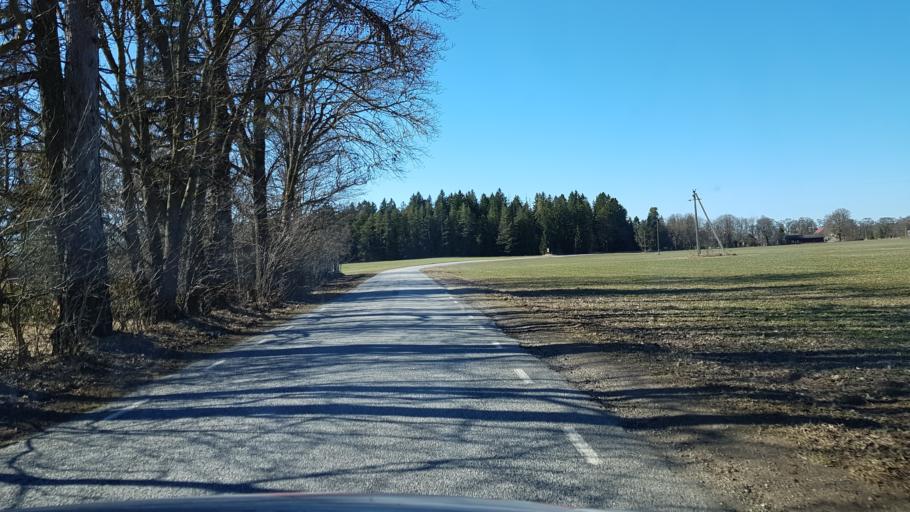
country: EE
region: Laeaene-Virumaa
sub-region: Viru-Nigula vald
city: Kunda
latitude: 59.4075
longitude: 26.5343
